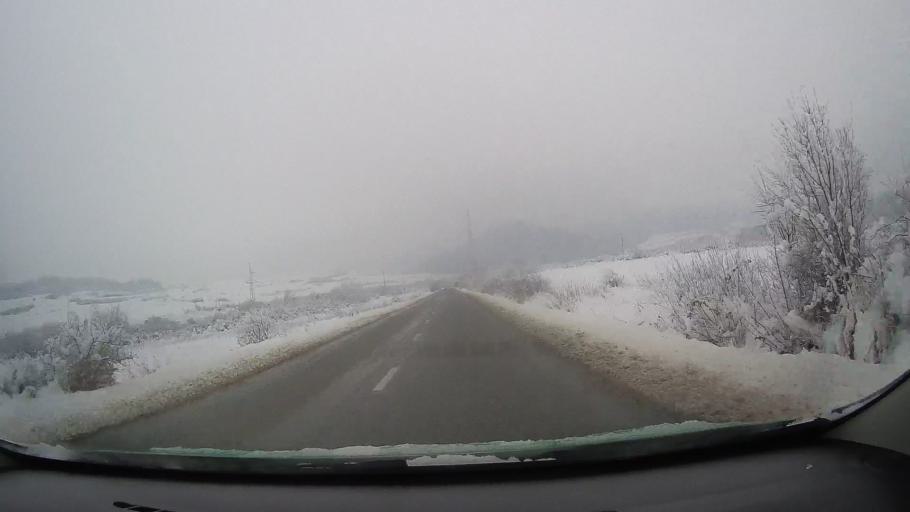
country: RO
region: Sibiu
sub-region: Comuna Orlat
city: Orlat
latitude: 45.7762
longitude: 23.9455
